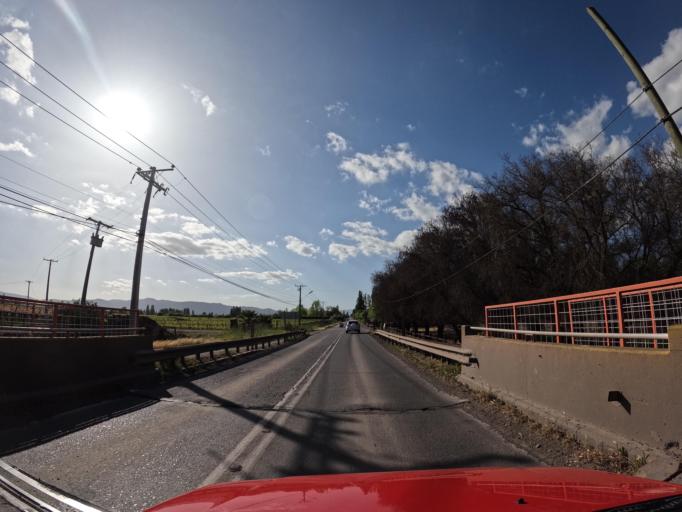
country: CL
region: Maule
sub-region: Provincia de Curico
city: Curico
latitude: -34.9554
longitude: -71.2541
